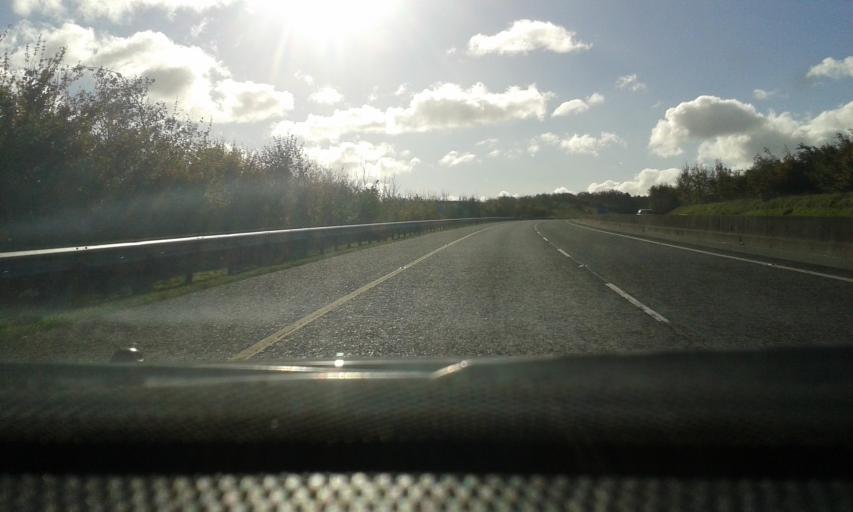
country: IE
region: Munster
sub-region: County Cork
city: Fermoy
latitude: 52.1293
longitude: -8.2600
